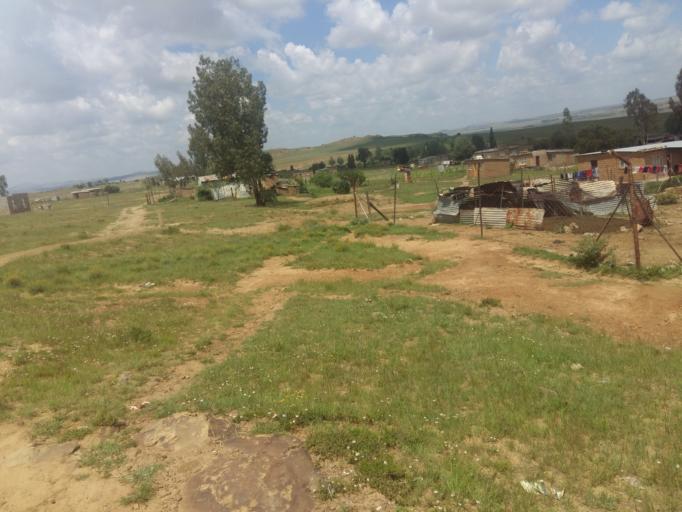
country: LS
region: Mafeteng
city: Mafeteng
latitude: -29.7573
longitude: 27.1150
